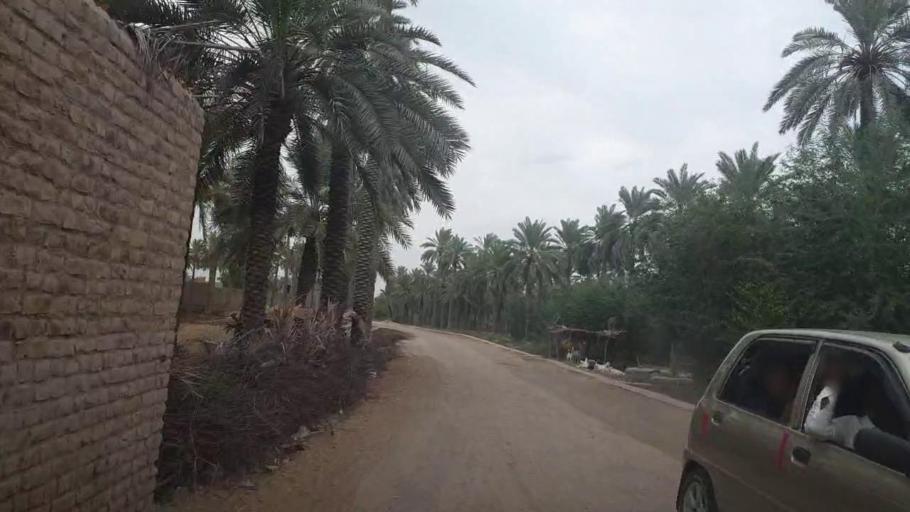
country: PK
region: Sindh
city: Khairpur
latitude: 27.5777
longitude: 68.7086
